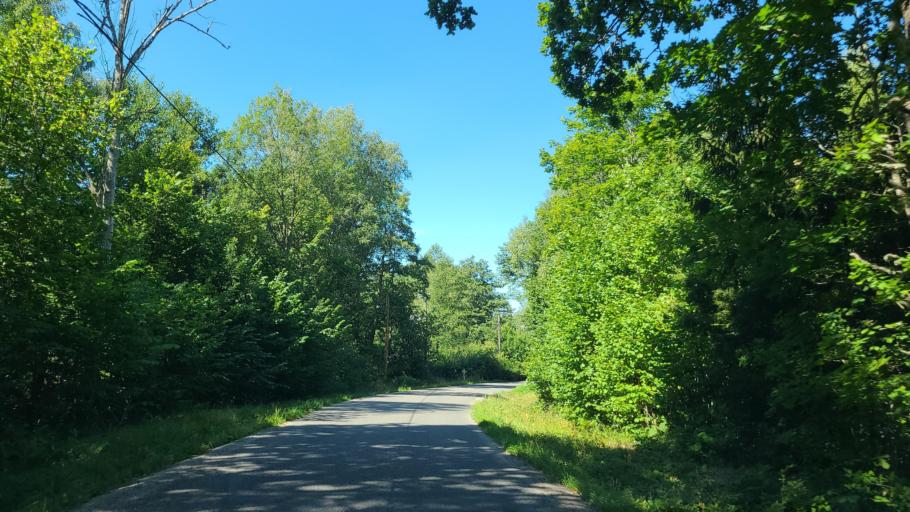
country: SE
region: Kalmar
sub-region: Kalmar Kommun
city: Ljungbyholm
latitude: 56.5738
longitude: 16.0205
